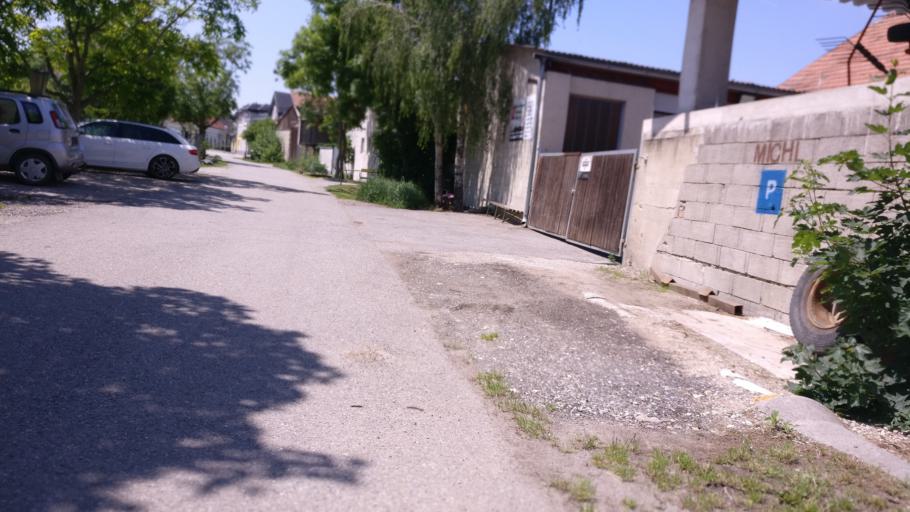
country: AT
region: Lower Austria
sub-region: Politischer Bezirk Baden
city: Schonau an der Triesting
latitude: 47.9349
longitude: 16.2561
